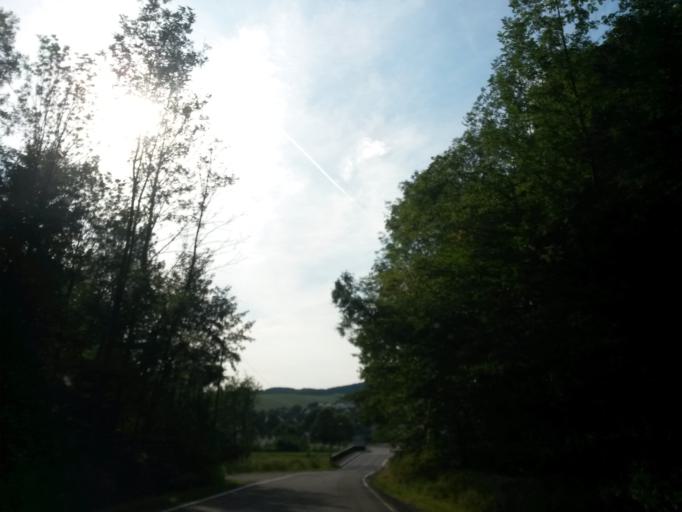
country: DE
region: North Rhine-Westphalia
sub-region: Regierungsbezirk Koln
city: Overath
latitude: 50.9598
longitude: 7.3255
